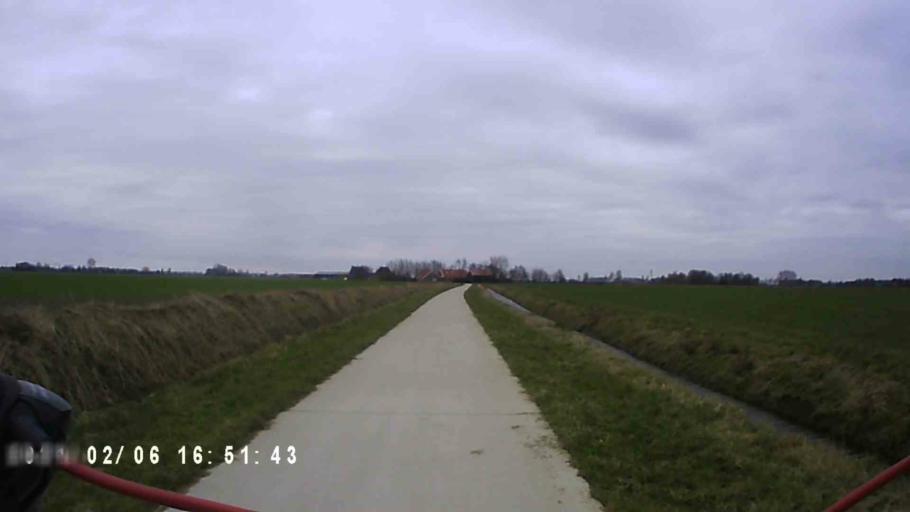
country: NL
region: Groningen
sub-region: Gemeente Appingedam
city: Appingedam
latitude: 53.4126
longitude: 6.7426
